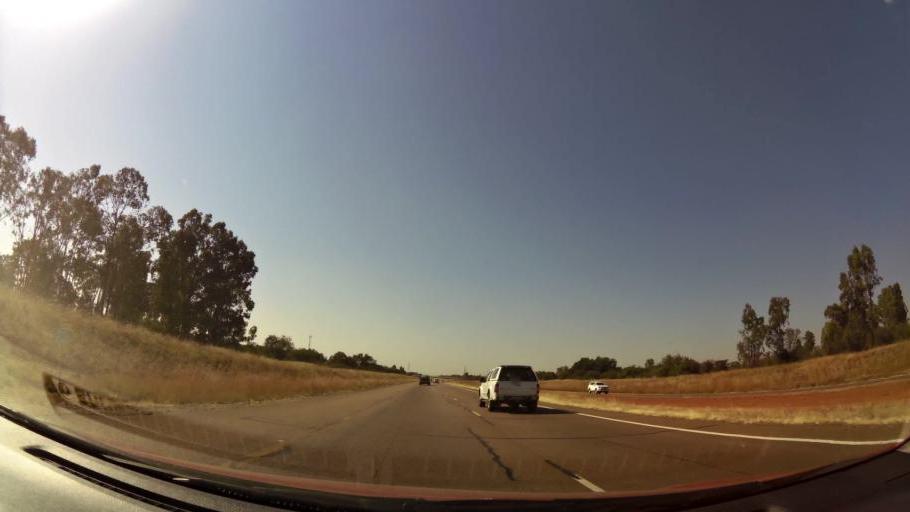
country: ZA
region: North-West
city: Ga-Rankuwa
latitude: -25.6576
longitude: 28.0751
